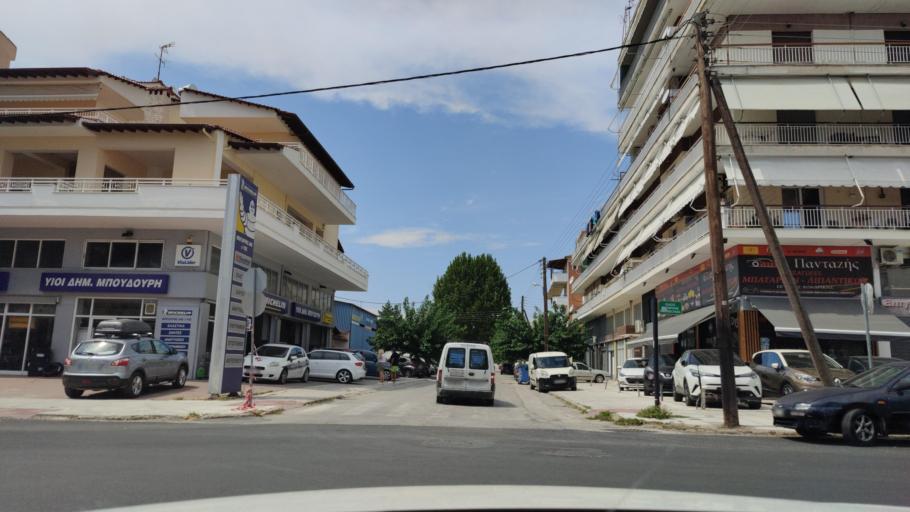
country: GR
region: Central Macedonia
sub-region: Nomos Serron
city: Serres
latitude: 41.0812
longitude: 23.5419
